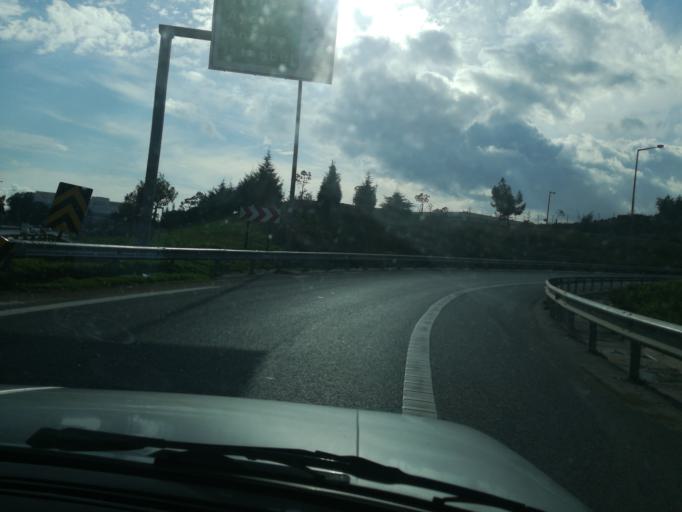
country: TR
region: Izmir
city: Gaziemir
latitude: 38.3454
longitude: 27.1308
